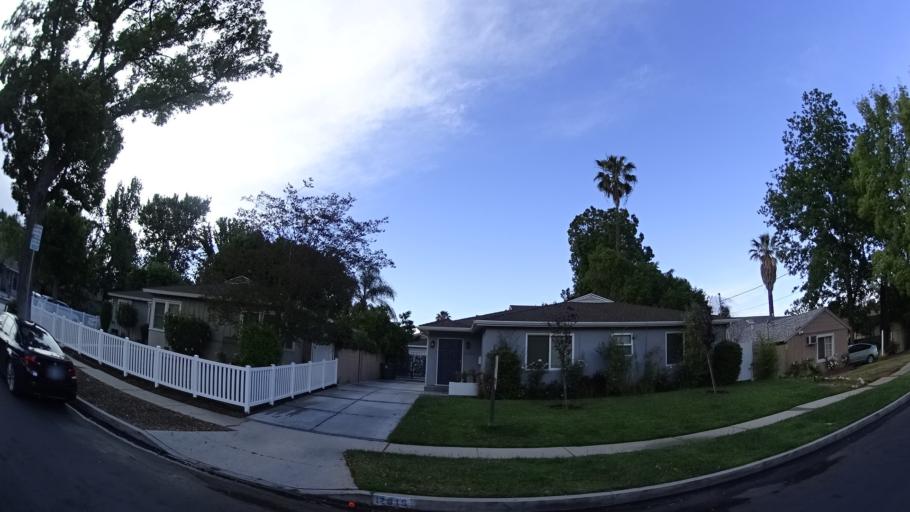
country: US
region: California
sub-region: Los Angeles County
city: North Hollywood
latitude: 34.1585
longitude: -118.4124
